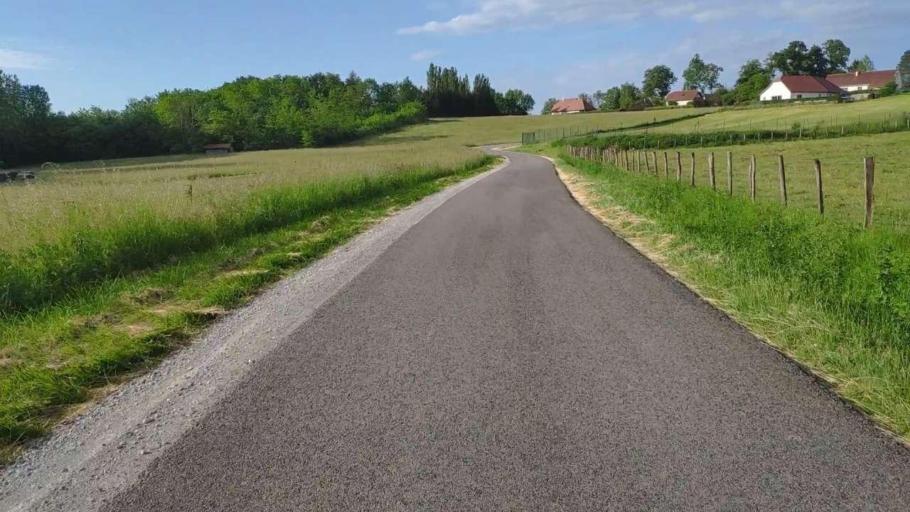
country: FR
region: Franche-Comte
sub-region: Departement du Jura
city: Bletterans
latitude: 46.7524
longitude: 5.4491
